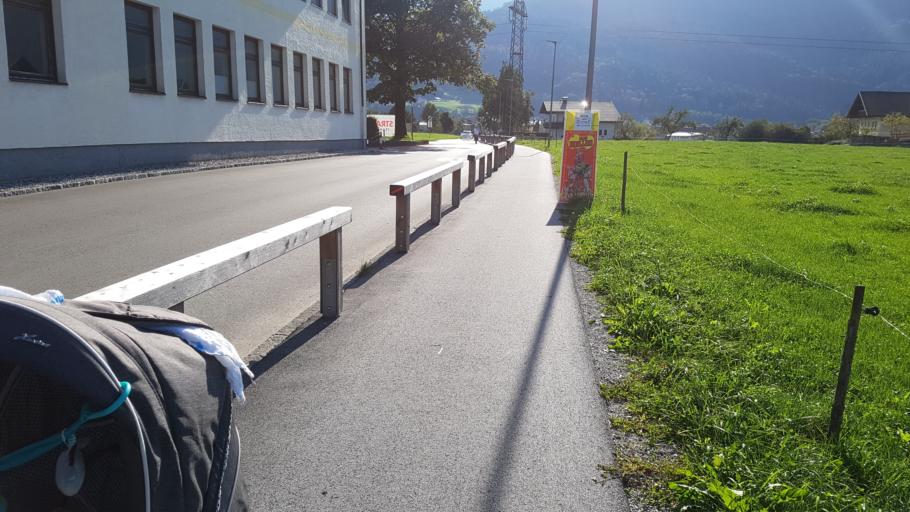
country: AT
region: Salzburg
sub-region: Politischer Bezirk Hallein
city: Kuchl
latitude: 47.6321
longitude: 13.1499
